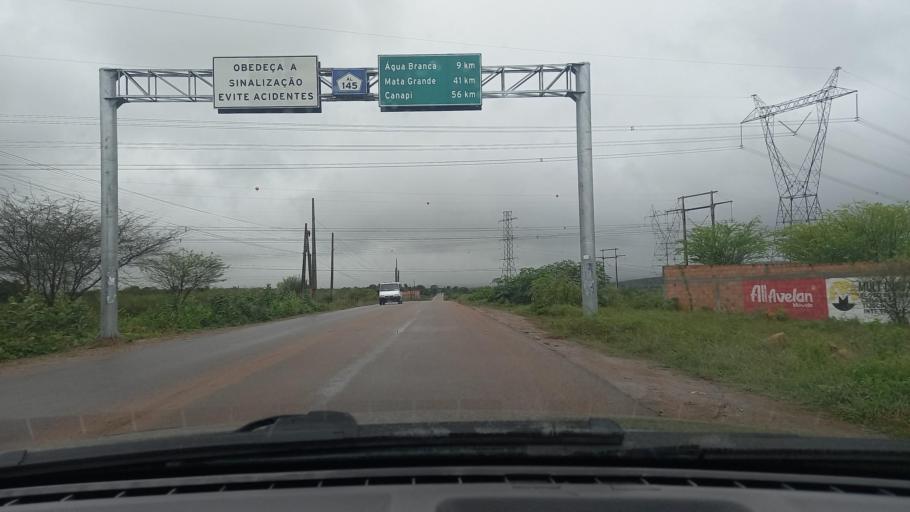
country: BR
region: Alagoas
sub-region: Delmiro Gouveia
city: Delmiro Gouveia
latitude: -9.3288
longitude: -37.9831
